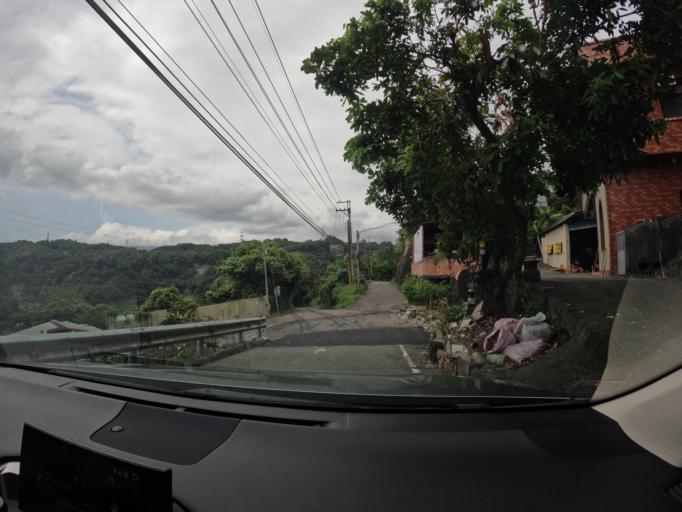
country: TW
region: Taiwan
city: Fengyuan
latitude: 24.3504
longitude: 120.8723
